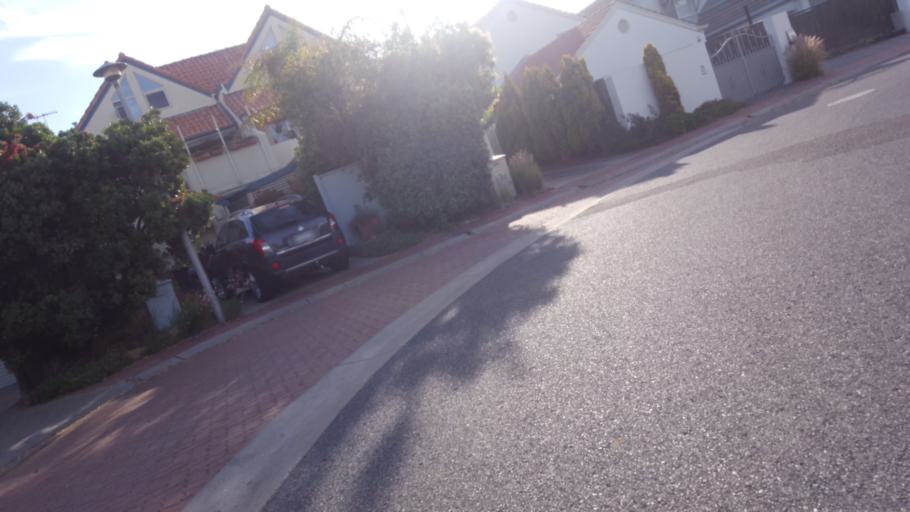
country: AU
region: South Australia
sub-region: Port Adelaide Enfield
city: Birkenhead
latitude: -34.7832
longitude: 138.4811
